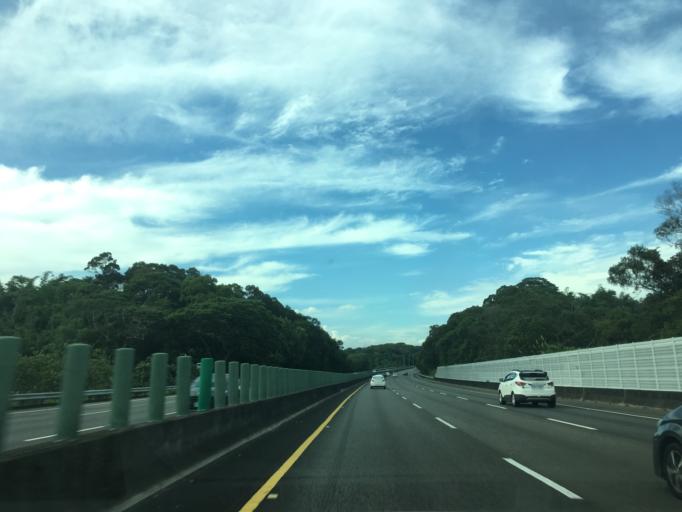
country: TW
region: Taiwan
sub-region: Chiayi
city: Jiayi Shi
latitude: 23.5695
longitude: 120.5055
